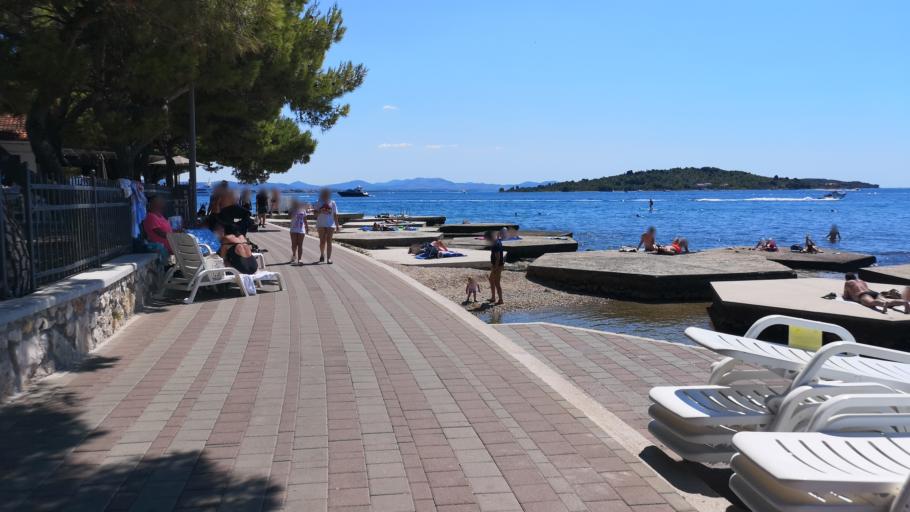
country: HR
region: Sibensko-Kniniska
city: Vodice
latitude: 43.7520
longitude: 15.7707
